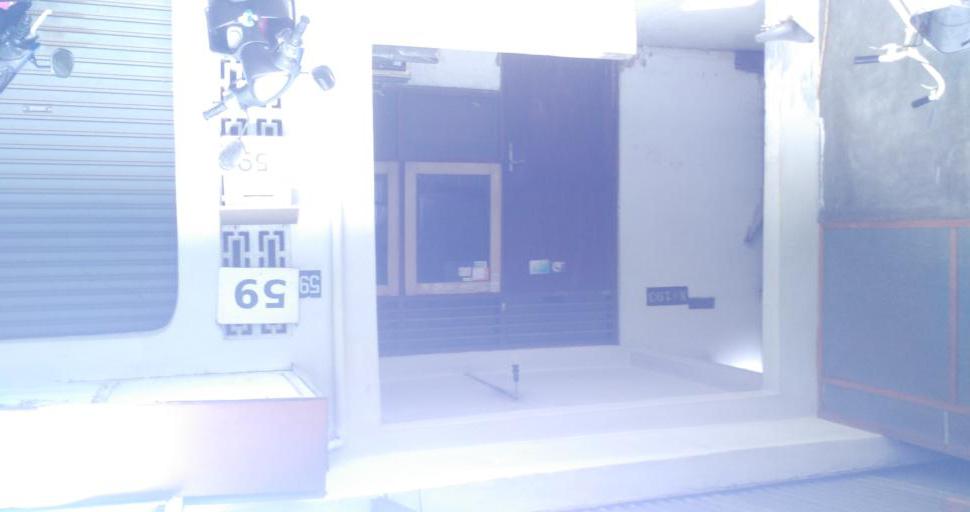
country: ID
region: Daerah Istimewa Yogyakarta
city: Yogyakarta
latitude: -7.8070
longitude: 110.3506
